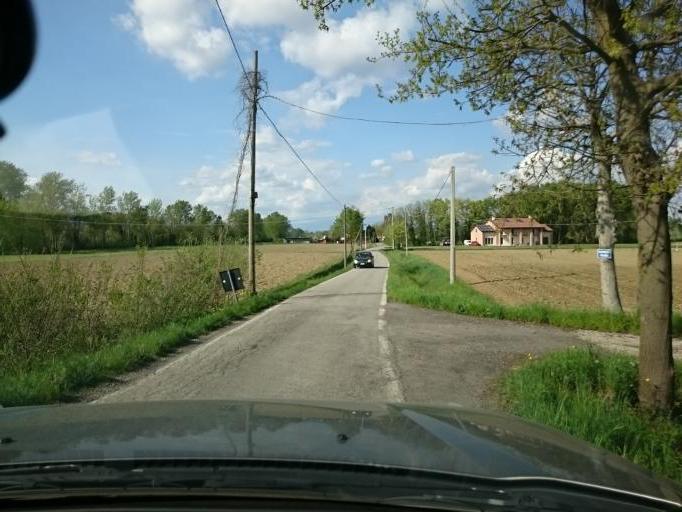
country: IT
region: Veneto
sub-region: Provincia di Padova
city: Torreselle
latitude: 45.6090
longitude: 12.0248
